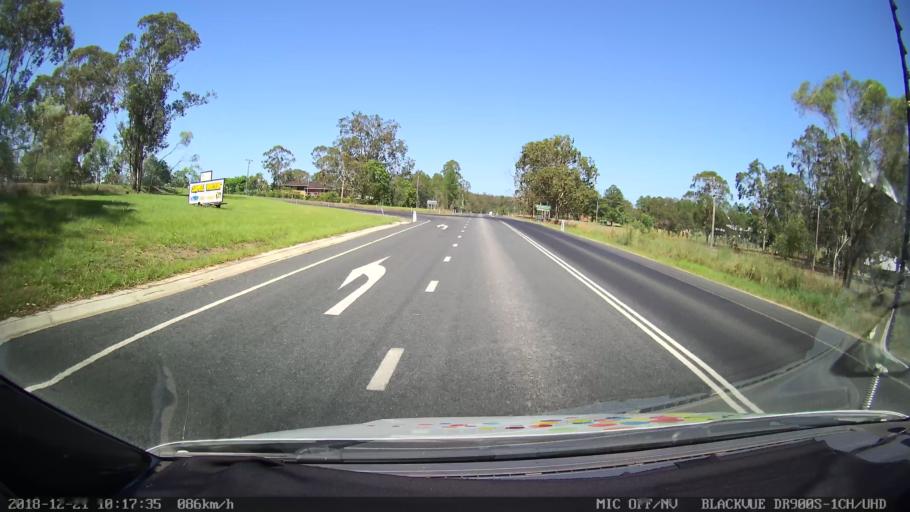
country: AU
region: New South Wales
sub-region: Clarence Valley
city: South Grafton
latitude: -29.6845
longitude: 152.8685
